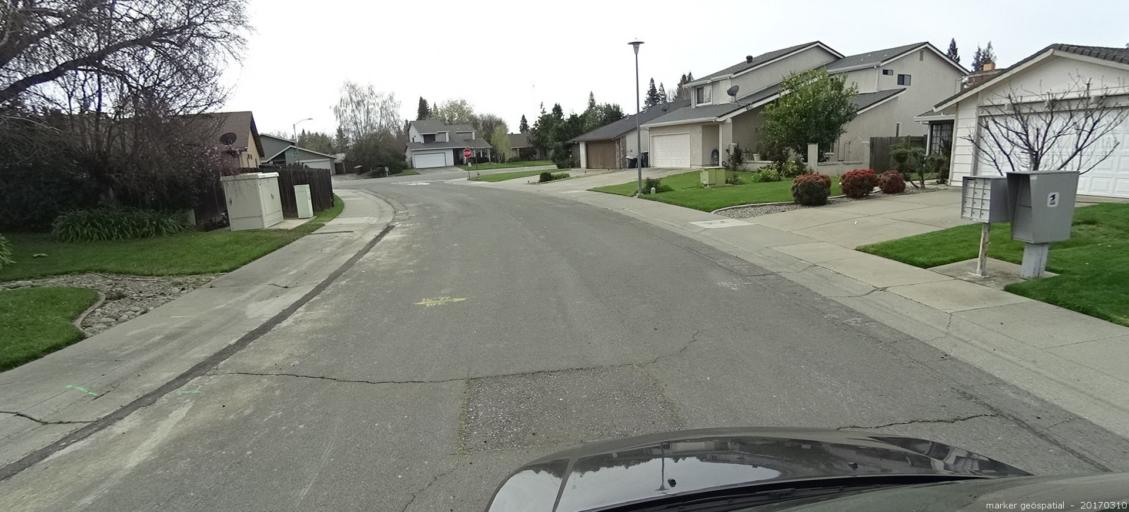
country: US
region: California
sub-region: Sacramento County
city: Parkway
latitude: 38.4898
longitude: -121.5267
